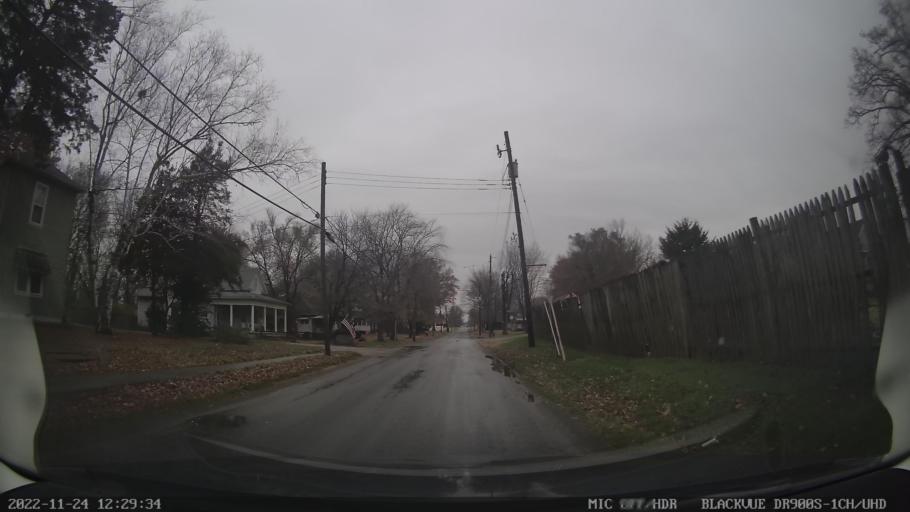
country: US
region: Illinois
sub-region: Macoupin County
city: Staunton
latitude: 39.0134
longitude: -89.7873
